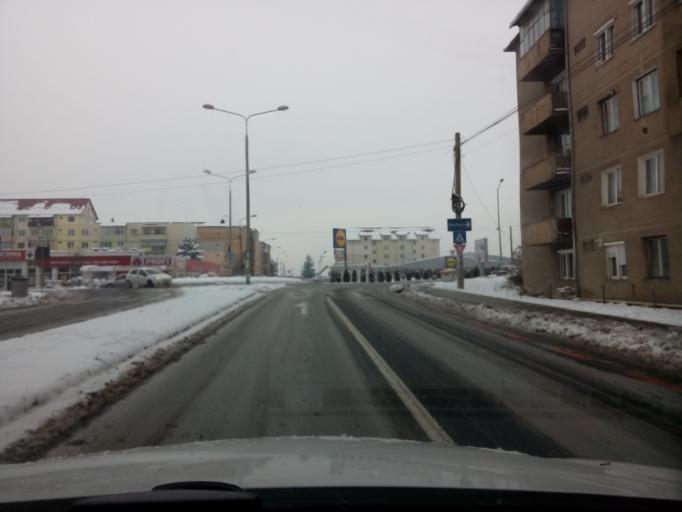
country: RO
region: Sibiu
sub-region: Municipiul Sibiu
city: Sibiu
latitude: 45.8094
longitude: 24.1478
